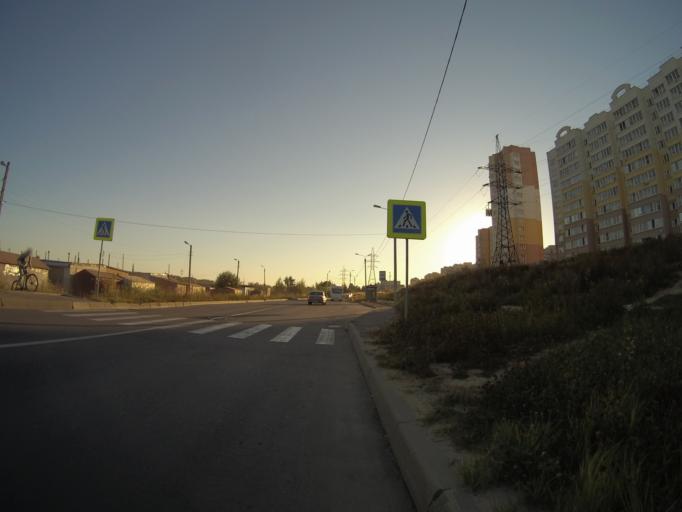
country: RU
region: Vladimir
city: Vladimir
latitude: 56.1036
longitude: 40.3620
